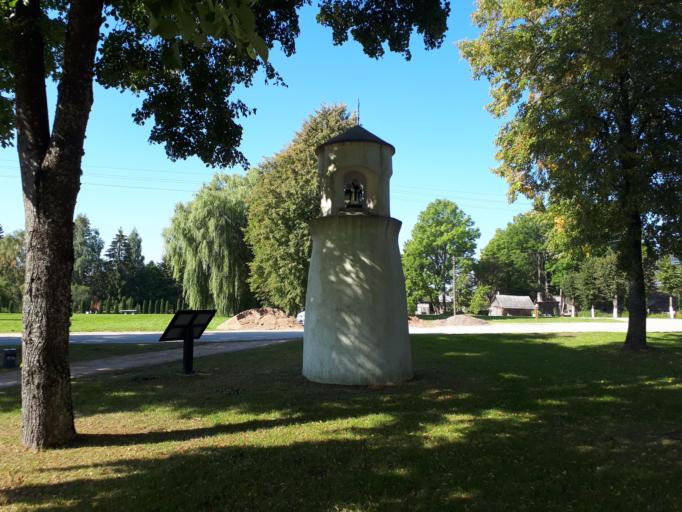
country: LV
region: Vainode
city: Vainode
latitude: 56.4181
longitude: 22.1089
